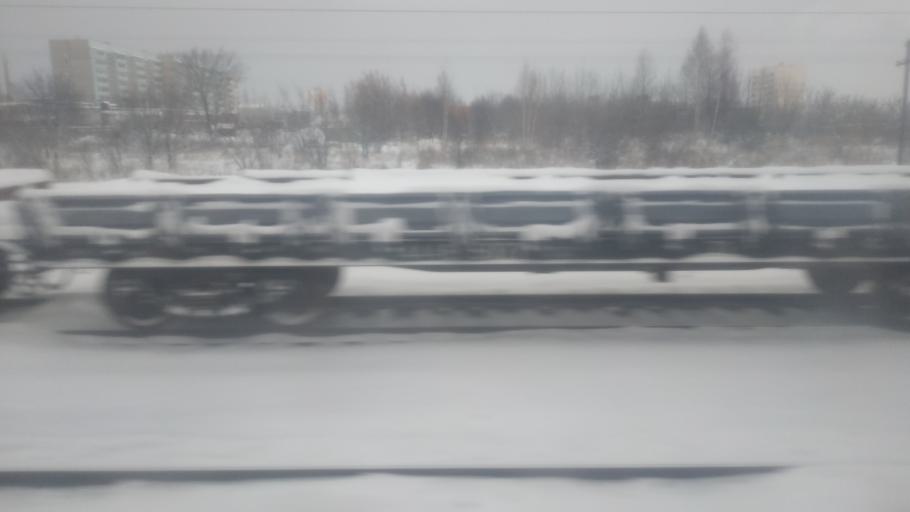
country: RU
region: Bashkortostan
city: Amzya
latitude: 56.2410
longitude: 54.5590
